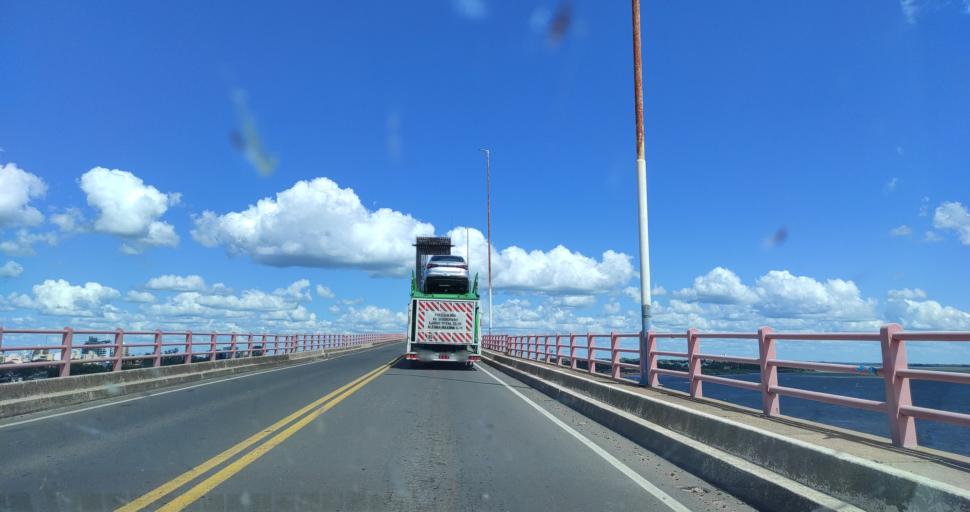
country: AR
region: Corrientes
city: Corrientes
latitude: -27.4676
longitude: -58.8629
